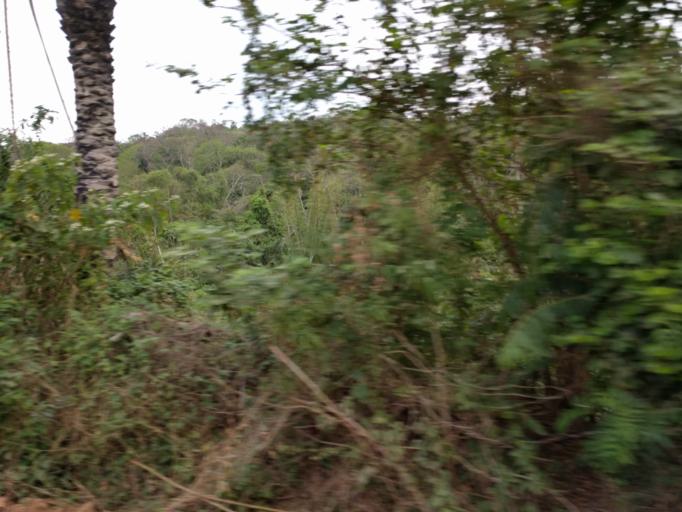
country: BO
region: Santa Cruz
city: Santa Rita
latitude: -17.9298
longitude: -63.3927
